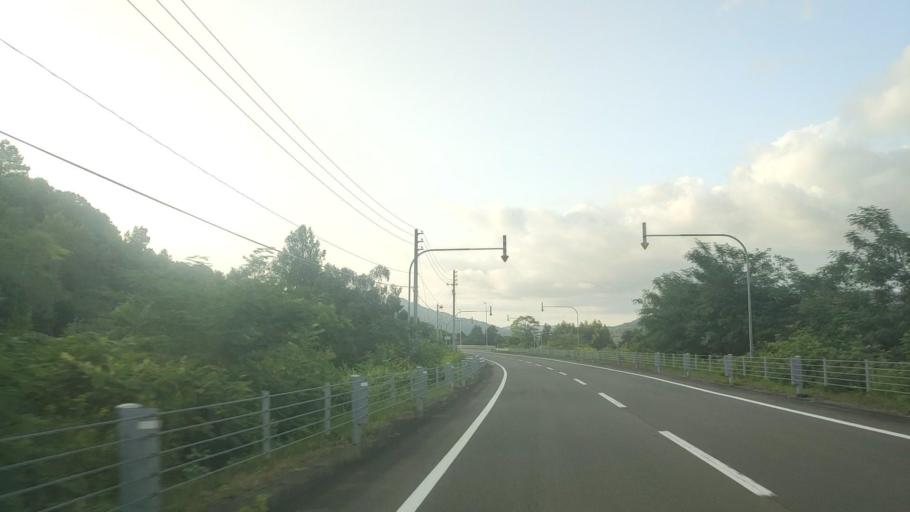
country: JP
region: Hokkaido
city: Bibai
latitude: 43.0771
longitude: 142.1019
